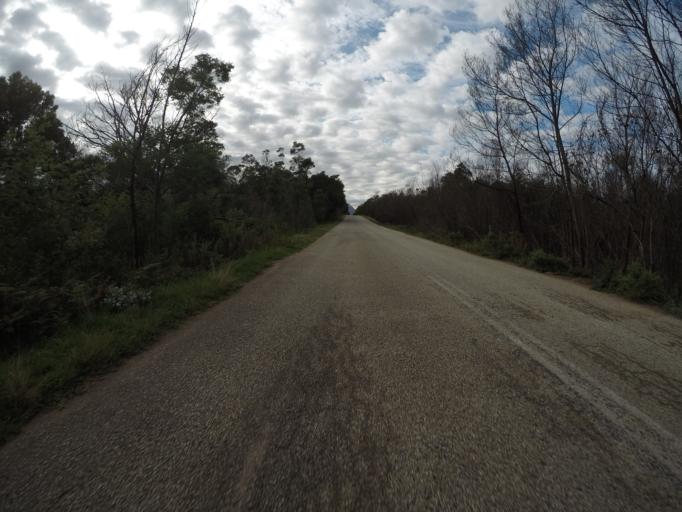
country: ZA
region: Eastern Cape
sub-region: Cacadu District Municipality
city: Kareedouw
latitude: -34.0160
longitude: 24.3313
